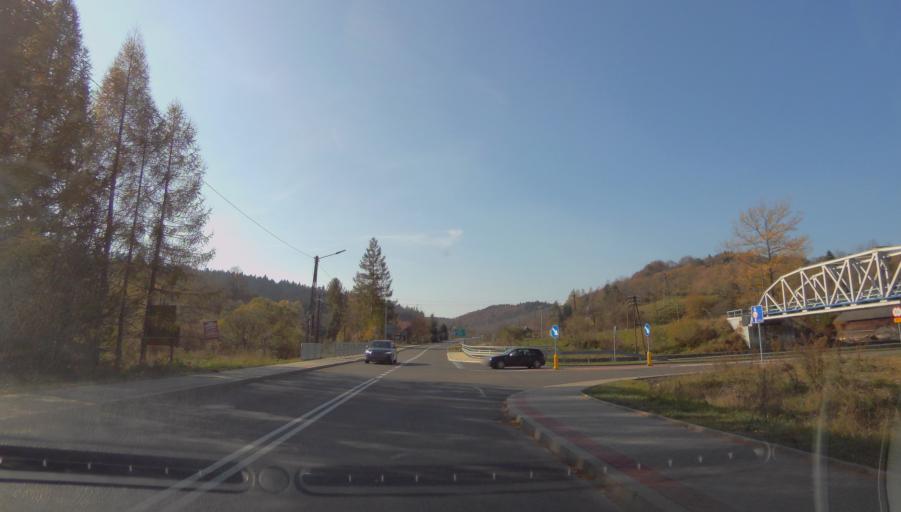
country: PL
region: Subcarpathian Voivodeship
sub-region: Powiat sanocki
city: Komancza
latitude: 49.3352
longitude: 22.0700
